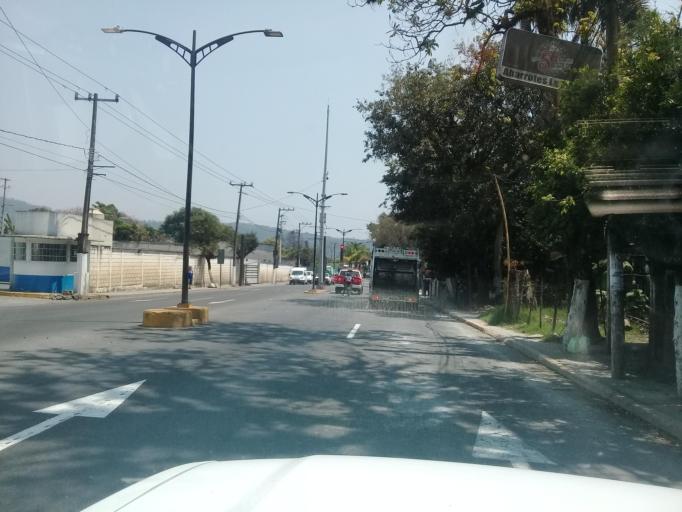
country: MX
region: Veracruz
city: Ixtac Zoquitlan
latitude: 18.8621
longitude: -97.0532
